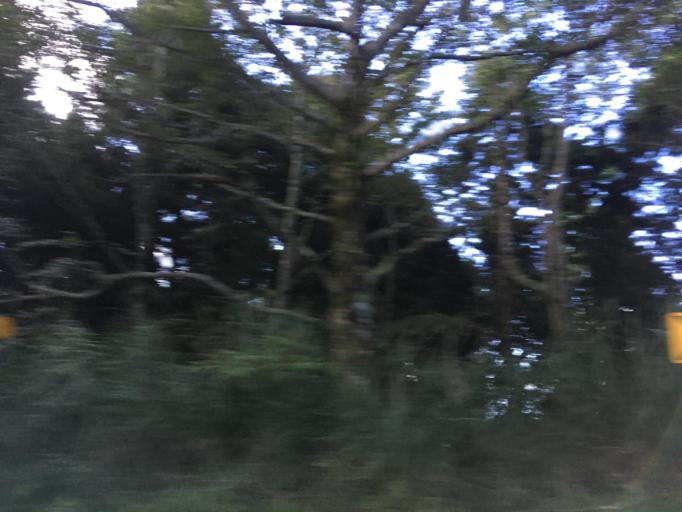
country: TW
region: Taiwan
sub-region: Yilan
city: Yilan
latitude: 24.5113
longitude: 121.5901
